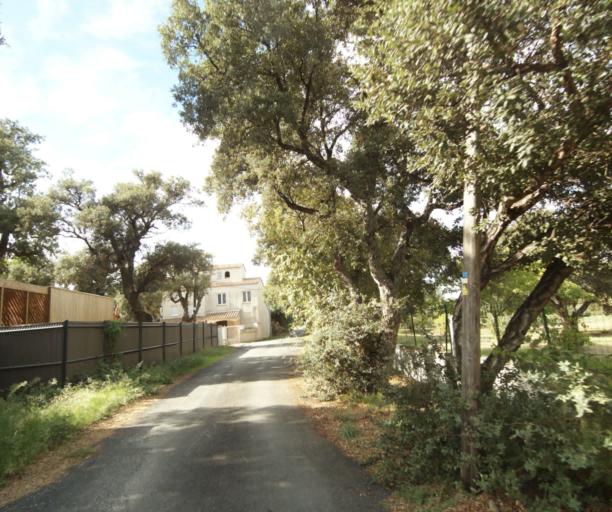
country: FR
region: Languedoc-Roussillon
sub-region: Departement des Pyrenees-Orientales
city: Sant Andreu de Sureda
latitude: 42.5398
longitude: 2.9955
